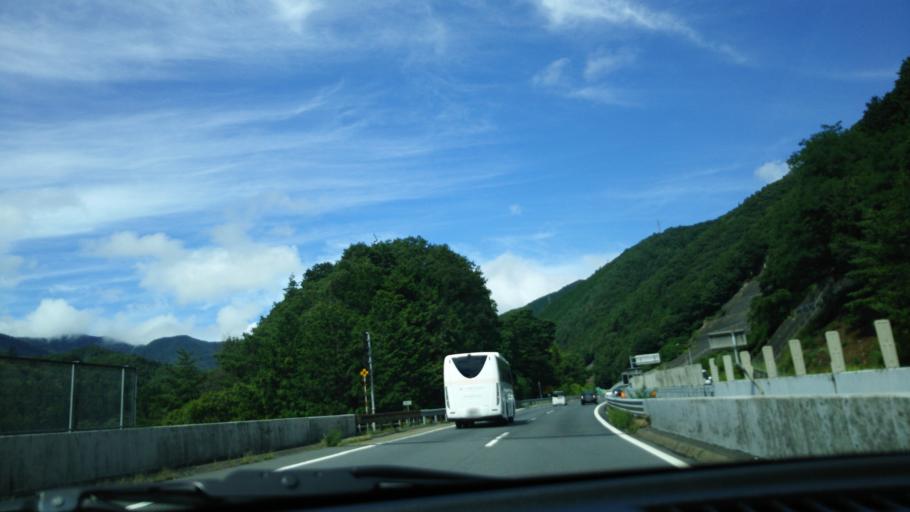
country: JP
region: Yamanashi
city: Otsuki
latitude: 35.6056
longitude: 138.8245
